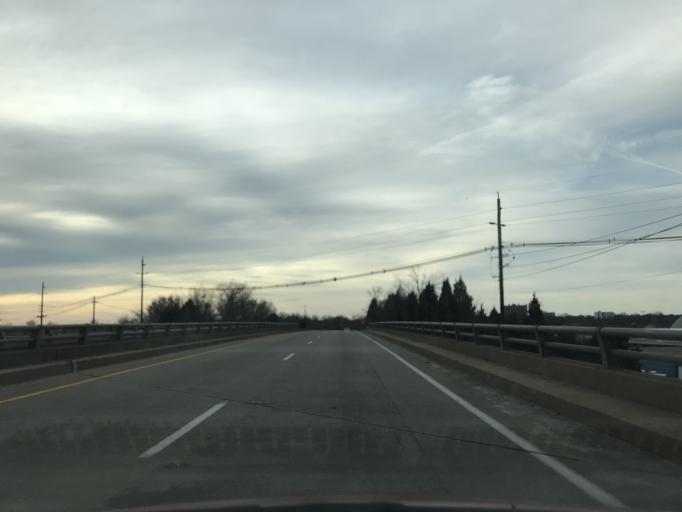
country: US
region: Kentucky
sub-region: Jefferson County
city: West Buechel
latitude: 38.1897
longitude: -85.6714
